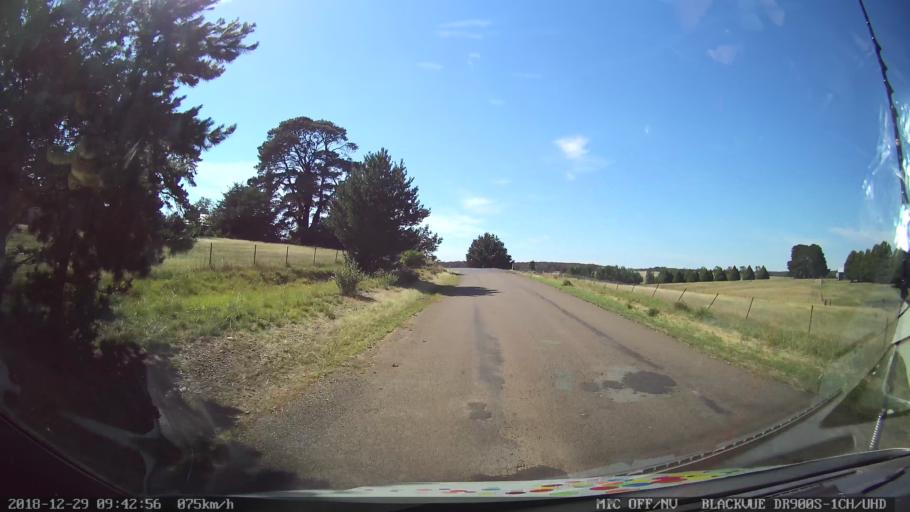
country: AU
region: New South Wales
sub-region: Upper Lachlan Shire
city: Crookwell
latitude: -34.6746
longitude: 149.4234
